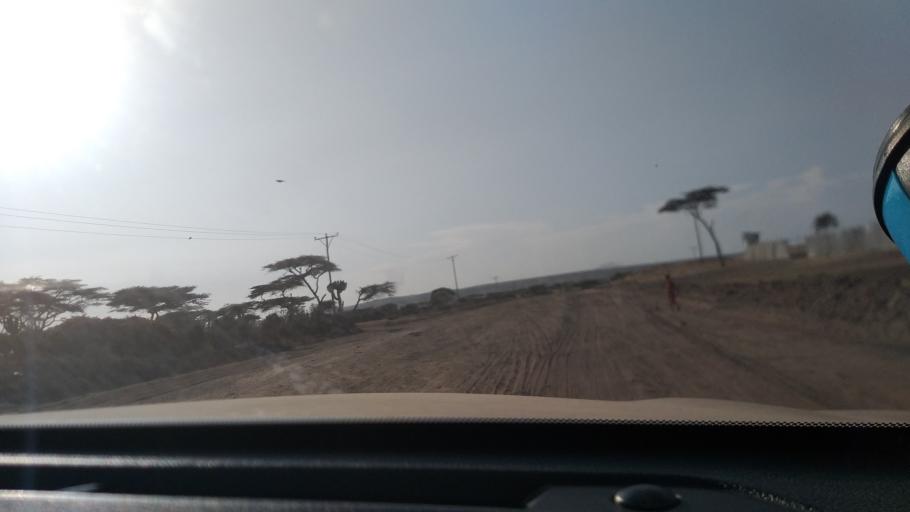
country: ET
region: Oromiya
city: Shashemene
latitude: 7.4983
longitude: 38.6974
